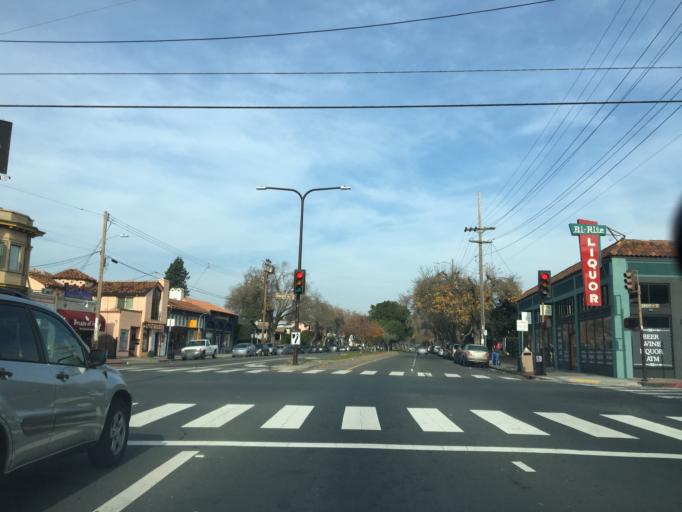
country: US
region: California
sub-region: Alameda County
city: Berkeley
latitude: 37.8620
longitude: -122.2810
